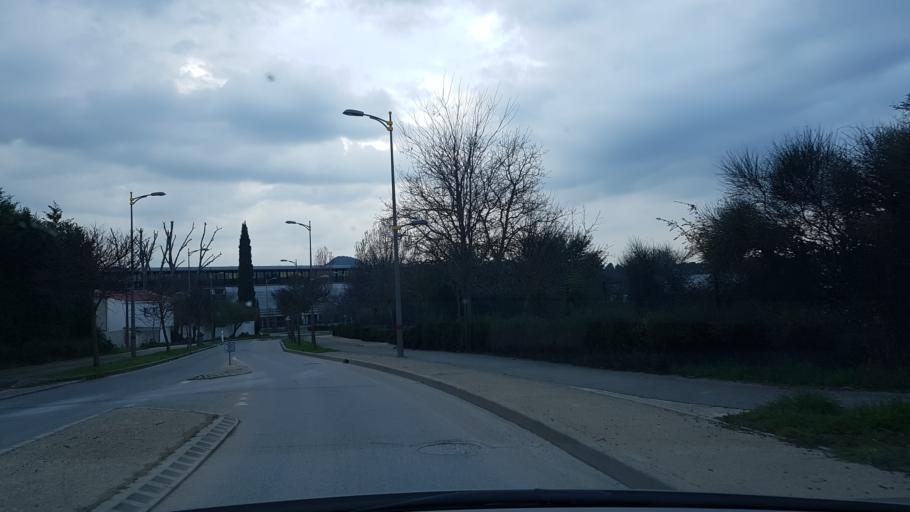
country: FR
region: Provence-Alpes-Cote d'Azur
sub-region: Departement des Bouches-du-Rhone
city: Gardanne
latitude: 43.4456
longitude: 5.4819
